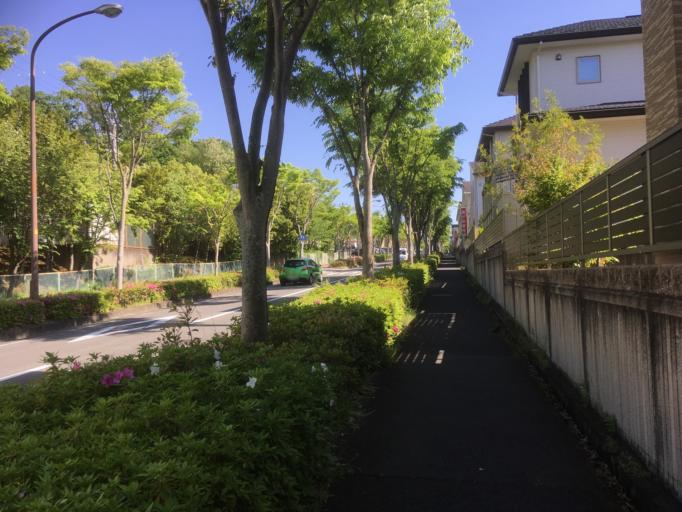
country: JP
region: Nara
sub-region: Ikoma-shi
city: Ikoma
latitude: 34.7248
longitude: 135.7158
